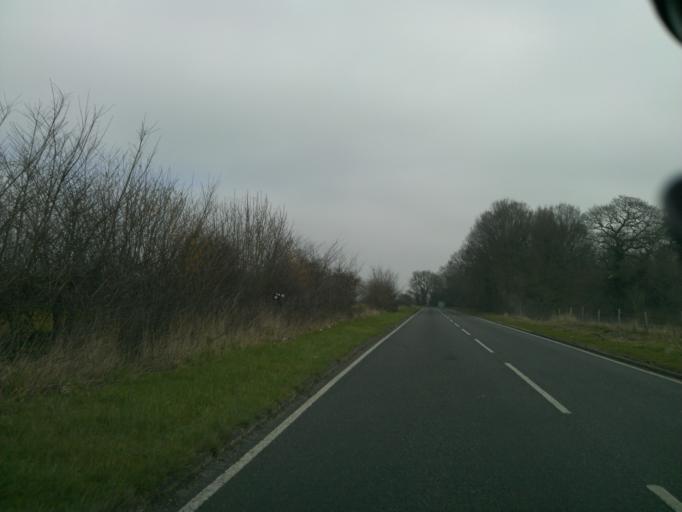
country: GB
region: England
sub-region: Essex
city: Rayne
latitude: 51.8406
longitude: 0.6101
